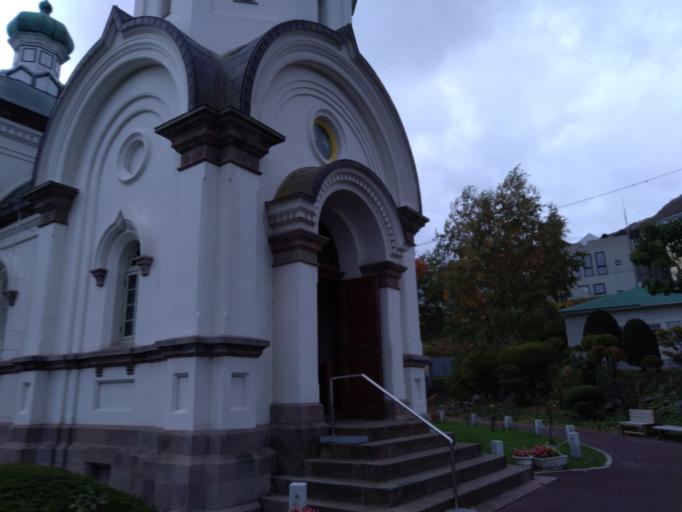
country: JP
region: Hokkaido
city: Hakodate
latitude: 41.7630
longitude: 140.7122
